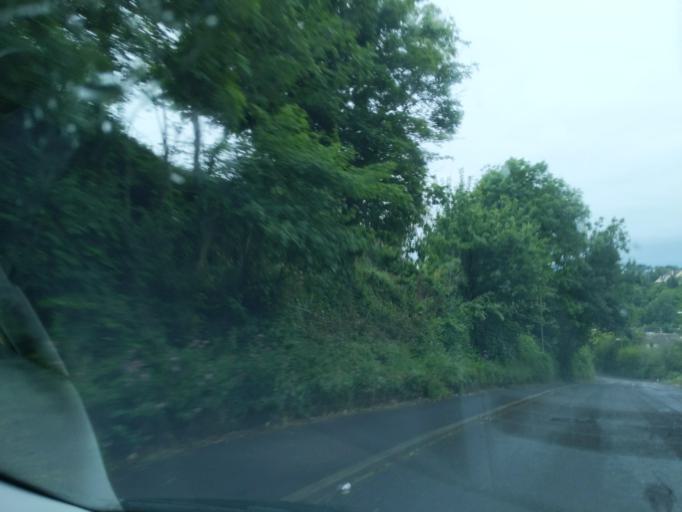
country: GB
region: England
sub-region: Borough of Torbay
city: Paignton
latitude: 50.4353
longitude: -3.5843
